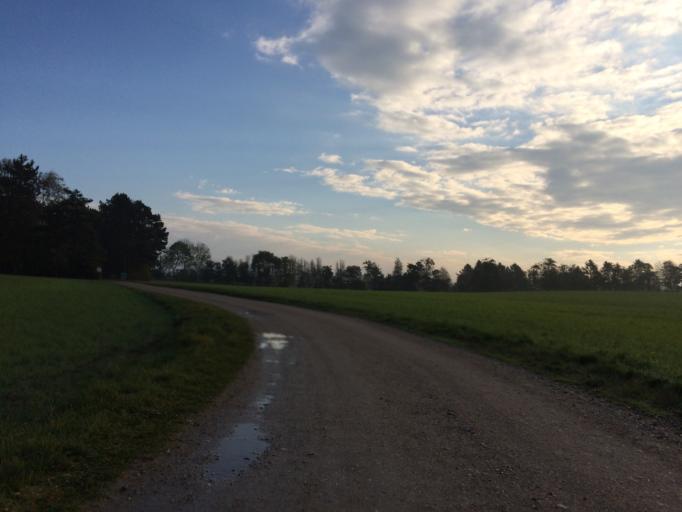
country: DK
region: Zealand
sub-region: Ringsted Kommune
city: Ringsted
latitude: 55.4847
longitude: 11.7438
